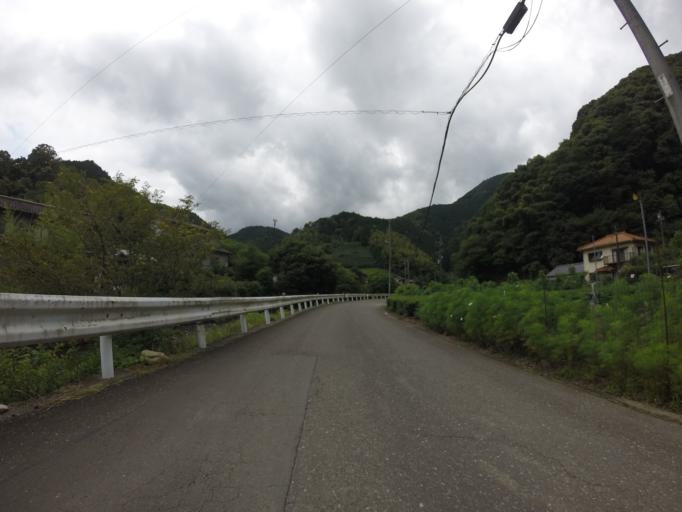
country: JP
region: Shizuoka
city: Shizuoka-shi
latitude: 35.0135
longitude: 138.3106
